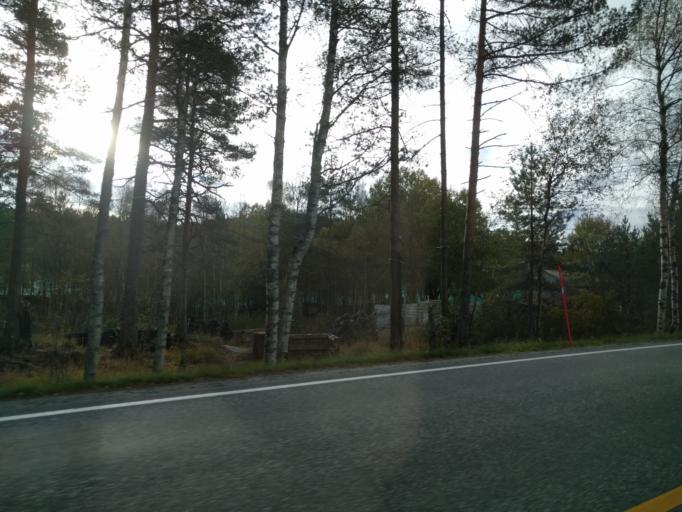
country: NO
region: Vest-Agder
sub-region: Songdalen
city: Nodeland
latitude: 58.2770
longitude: 7.8365
